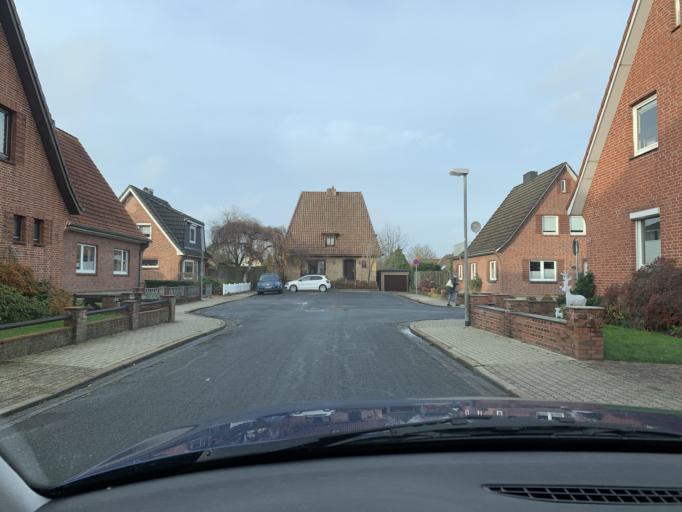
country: DE
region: Schleswig-Holstein
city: Wesseln
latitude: 54.2008
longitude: 9.0828
